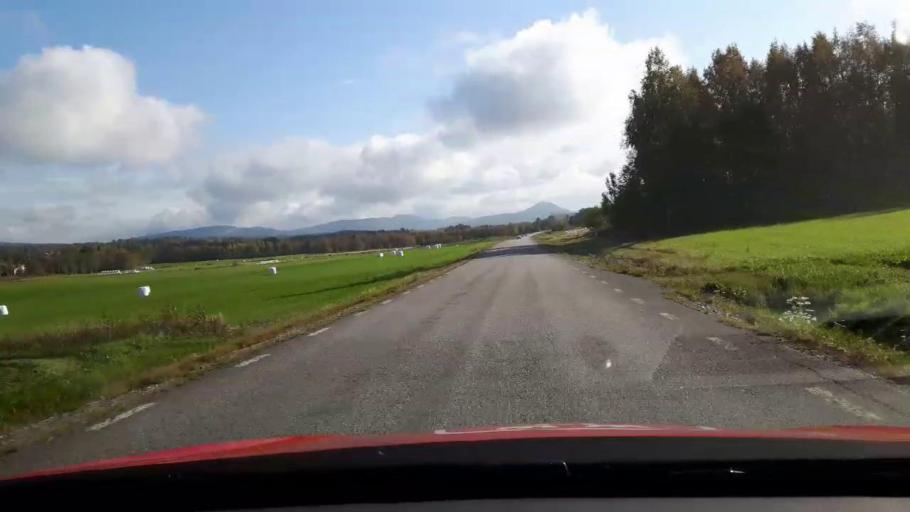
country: SE
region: Gaevleborg
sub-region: Ljusdals Kommun
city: Ljusdal
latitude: 61.7615
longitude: 16.0819
